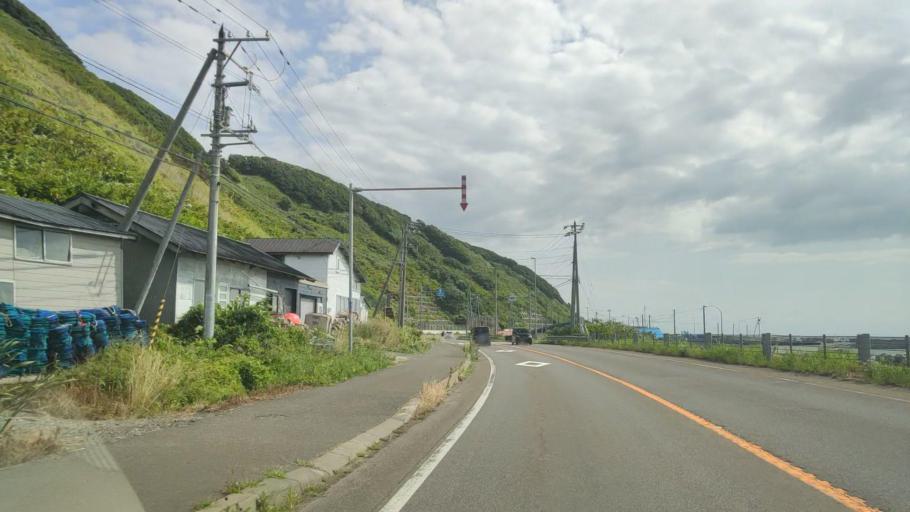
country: JP
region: Hokkaido
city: Rumoi
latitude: 44.2263
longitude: 141.6553
